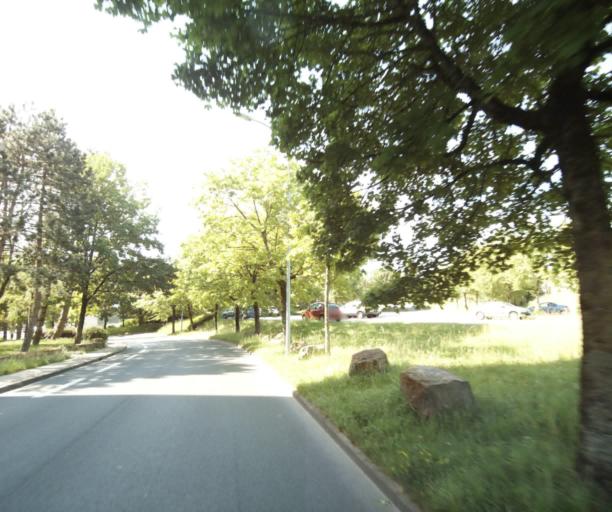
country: FR
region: Champagne-Ardenne
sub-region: Departement des Ardennes
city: La Francheville
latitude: 49.7419
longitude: 4.7230
